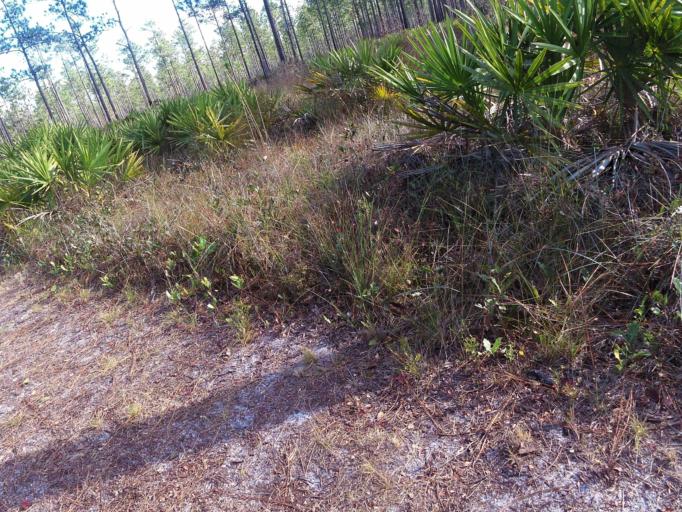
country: US
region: Florida
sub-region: Clay County
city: Middleburg
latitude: 30.1358
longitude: -81.9631
